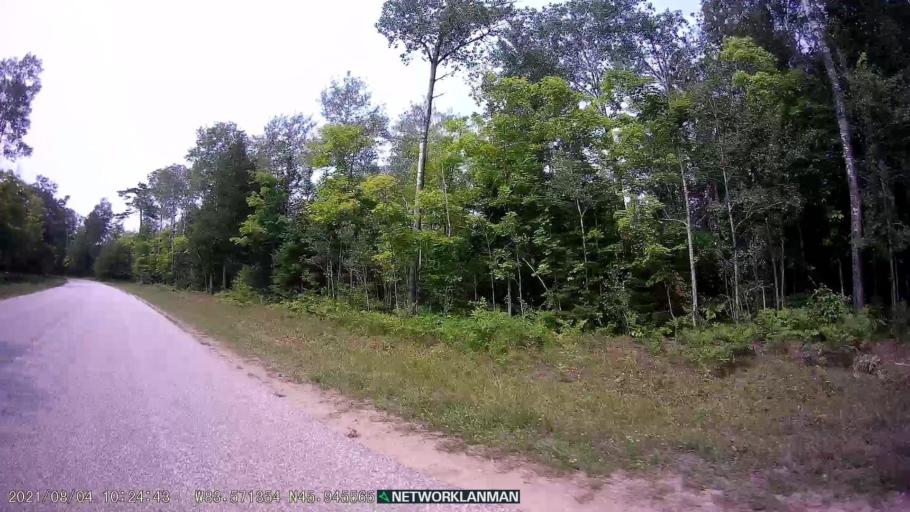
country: CA
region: Ontario
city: Thessalon
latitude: 45.9455
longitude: -83.5710
